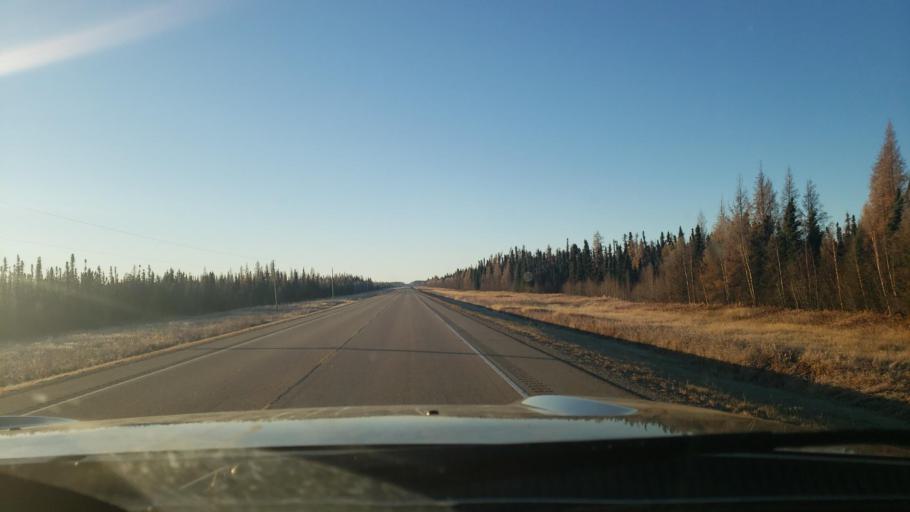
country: CA
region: British Columbia
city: Fort Nelson
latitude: 58.4730
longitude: -122.7138
